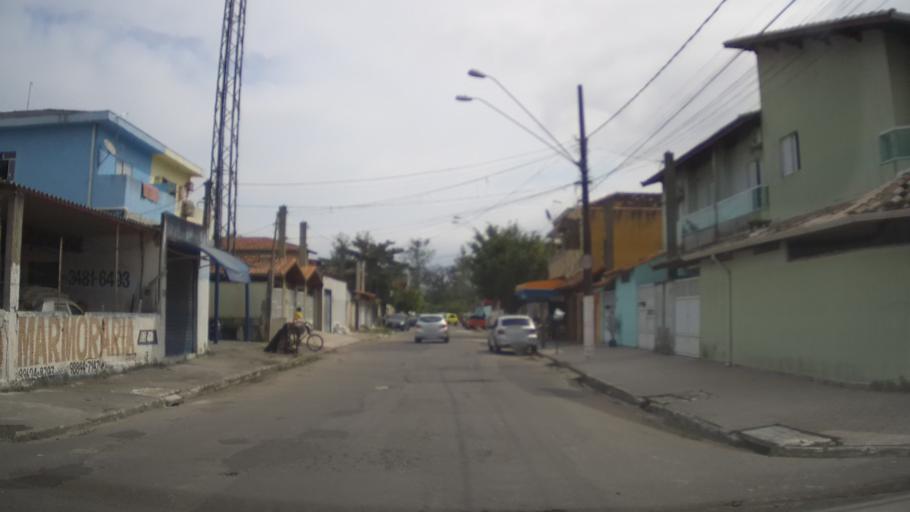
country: BR
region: Sao Paulo
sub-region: Praia Grande
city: Praia Grande
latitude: -24.0008
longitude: -46.4495
